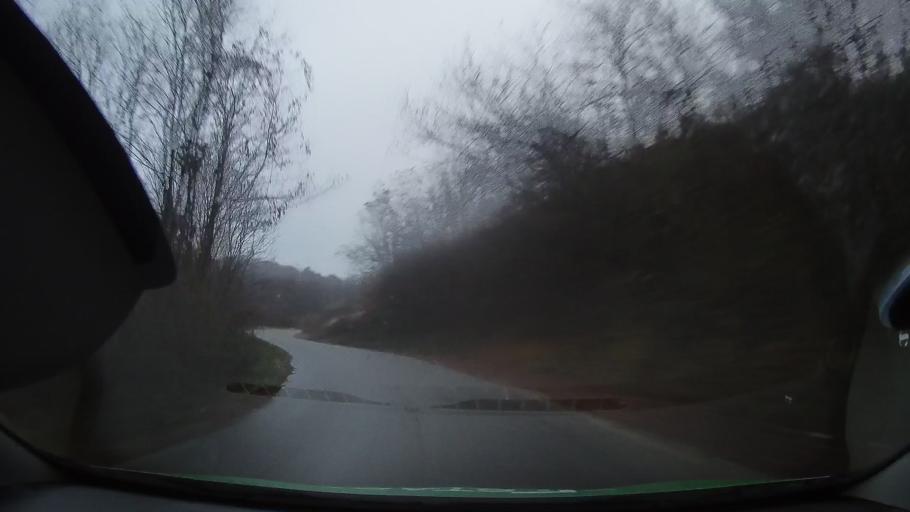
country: RO
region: Hunedoara
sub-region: Comuna Ribita
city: Ribita
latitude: 46.2354
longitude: 22.7466
